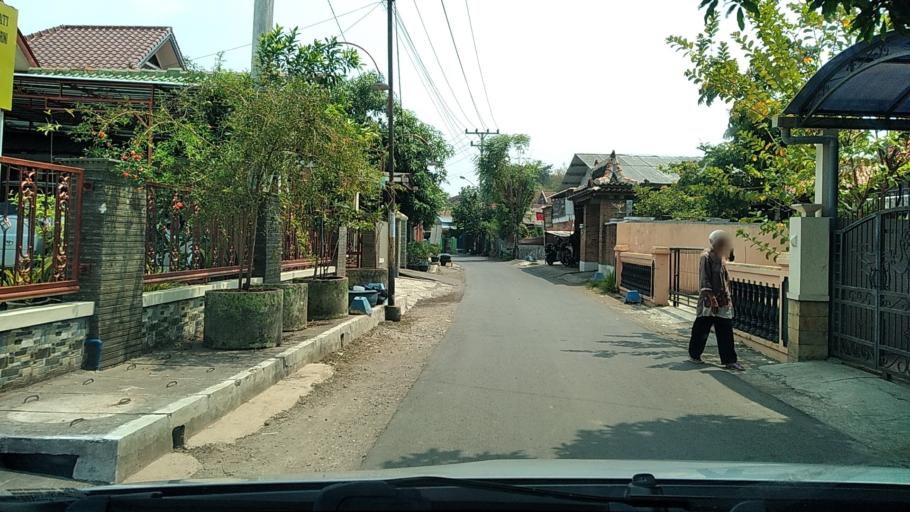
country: ID
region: Central Java
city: Semarang
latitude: -6.9851
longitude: 110.3630
